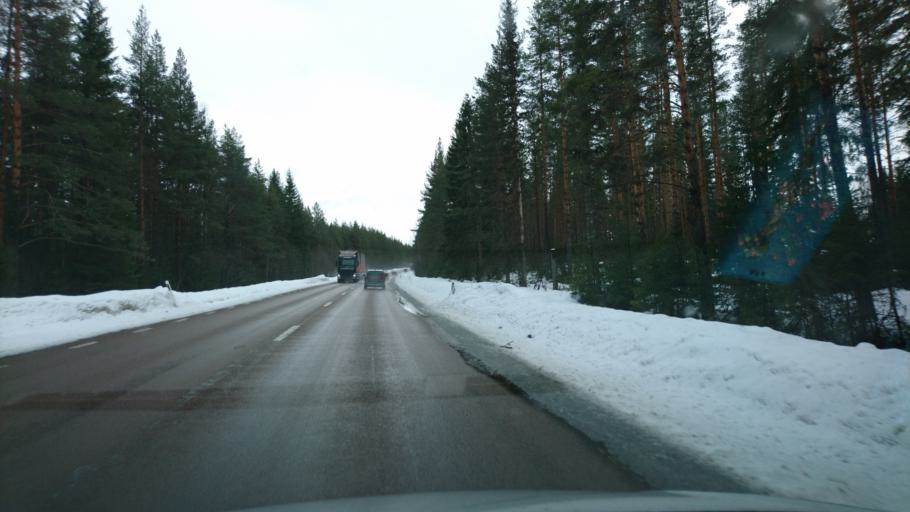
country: SE
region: Vaesternorrland
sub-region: Solleftea Kommun
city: Solleftea
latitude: 63.1025
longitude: 17.0117
